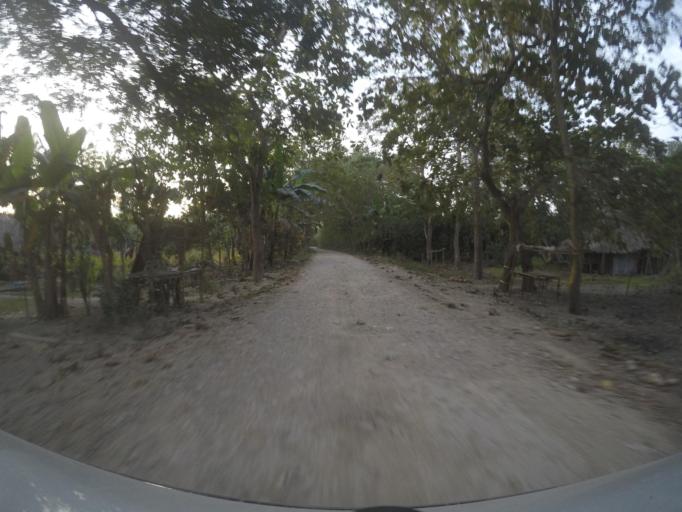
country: TL
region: Viqueque
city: Viqueque
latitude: -8.9340
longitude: 126.4125
